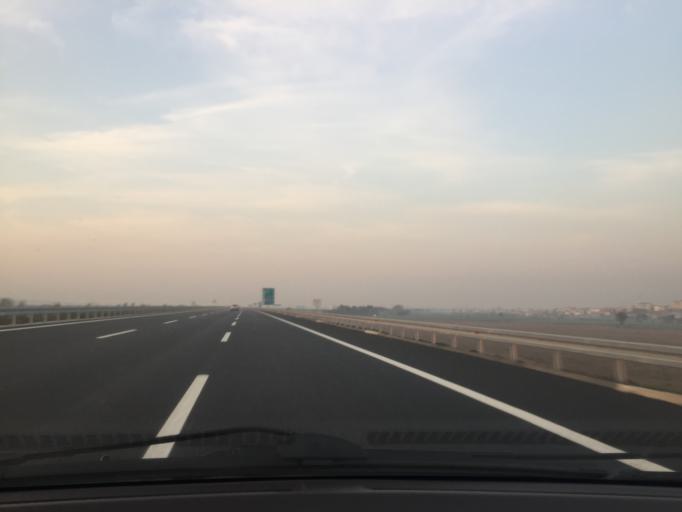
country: TR
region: Bursa
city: Karacabey
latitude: 40.2056
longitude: 28.3799
